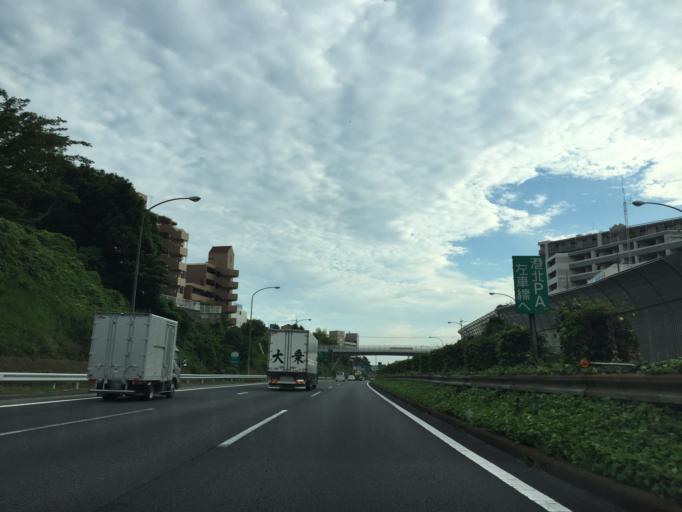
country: JP
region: Tokyo
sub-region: Machida-shi
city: Machida
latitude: 35.5512
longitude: 139.5474
